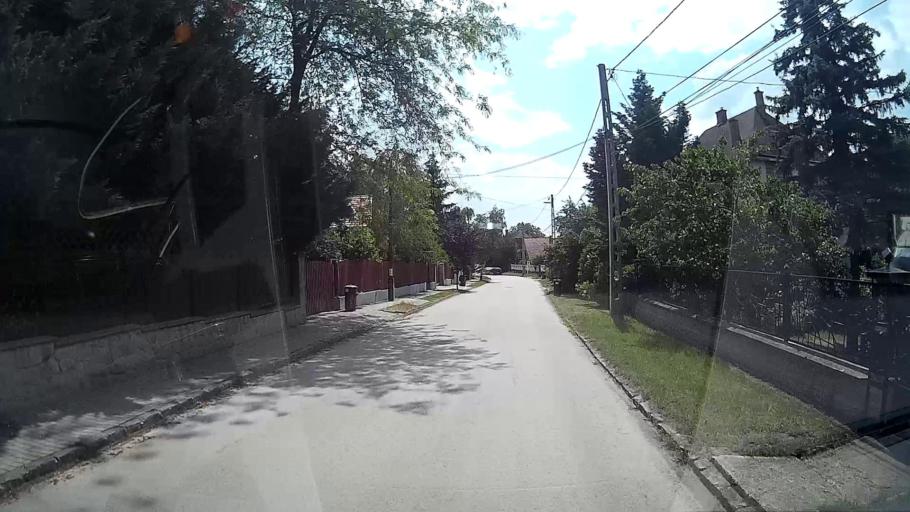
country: HU
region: Pest
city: Szentendre
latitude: 47.6717
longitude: 19.0671
